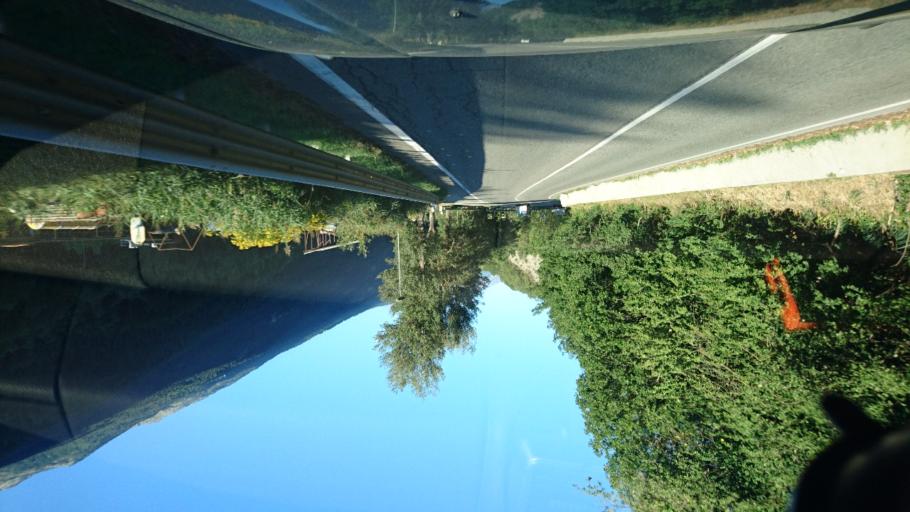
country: IT
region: Aosta Valley
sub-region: Valle d'Aosta
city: La Salle
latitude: 45.7417
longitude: 7.0649
